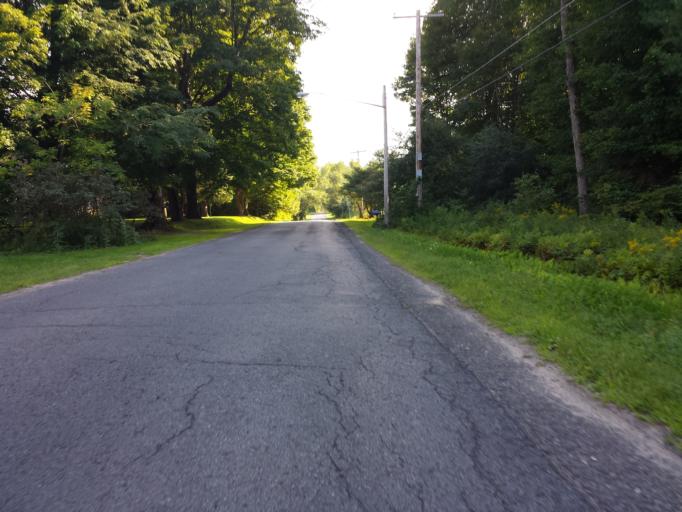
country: US
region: New York
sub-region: St. Lawrence County
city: Potsdam
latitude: 44.7119
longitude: -74.9028
